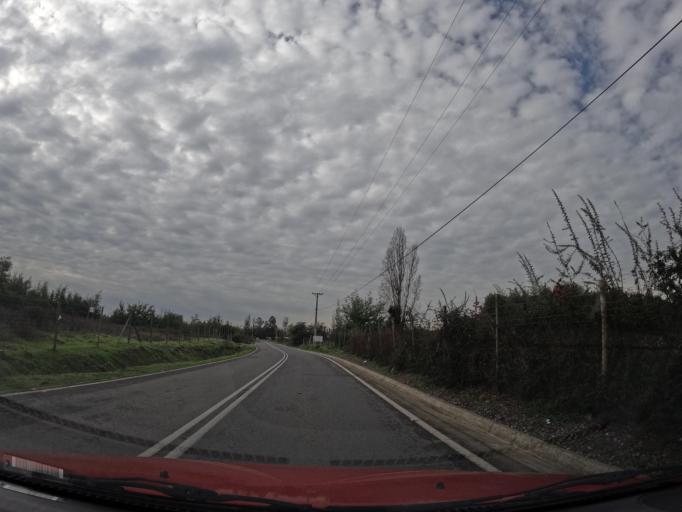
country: CL
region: Maule
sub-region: Provincia de Linares
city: Linares
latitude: -35.8644
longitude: -71.6197
